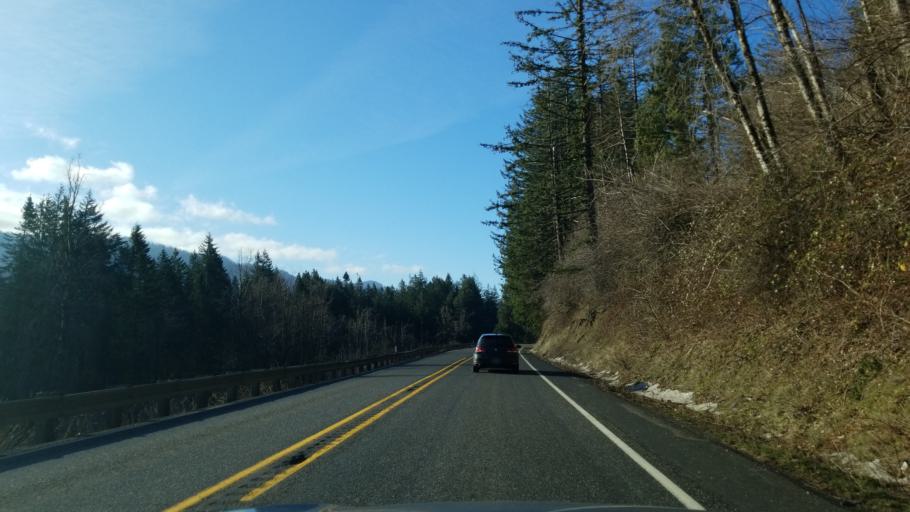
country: US
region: Oregon
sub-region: Hood River County
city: Cascade Locks
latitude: 45.6119
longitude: -122.0576
